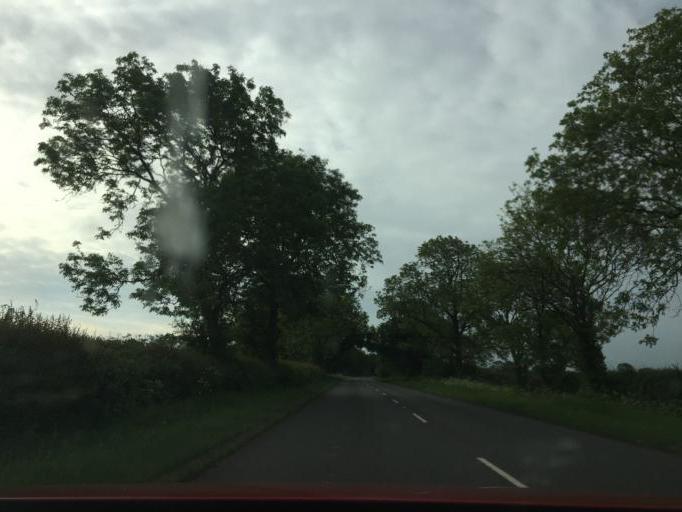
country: GB
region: England
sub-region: Leicestershire
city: Hinckley
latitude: 52.4805
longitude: -1.3317
